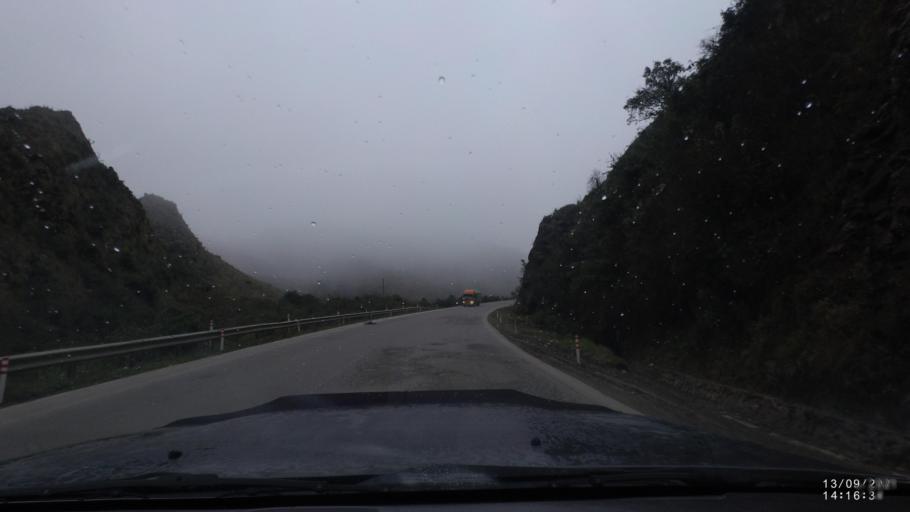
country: BO
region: Cochabamba
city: Colomi
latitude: -17.2167
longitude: -65.8916
